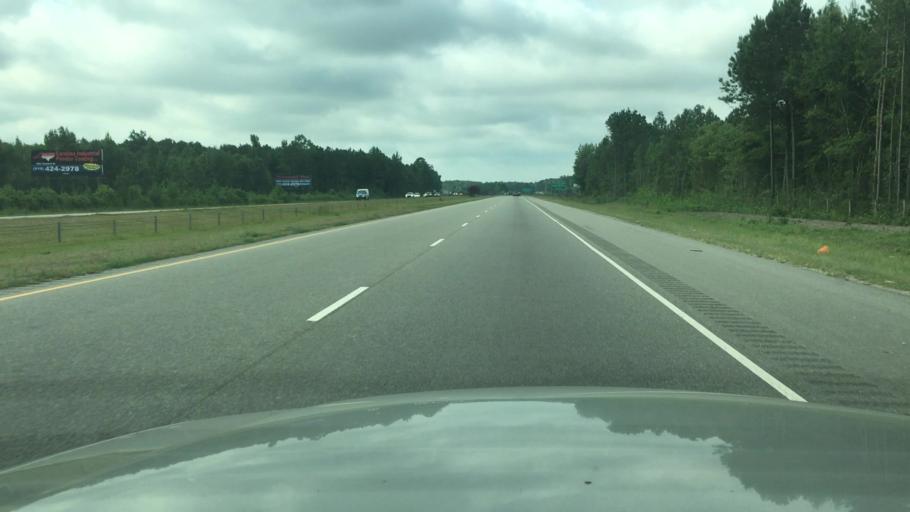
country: US
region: North Carolina
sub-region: Cumberland County
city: Fayetteville
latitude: 35.0228
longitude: -78.8722
